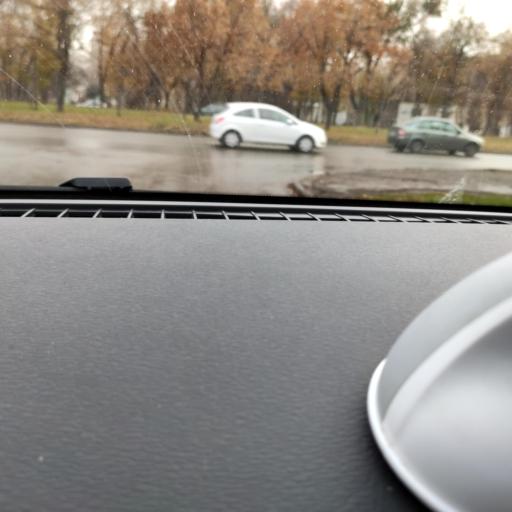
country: RU
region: Samara
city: Samara
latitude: 53.2196
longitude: 50.2391
